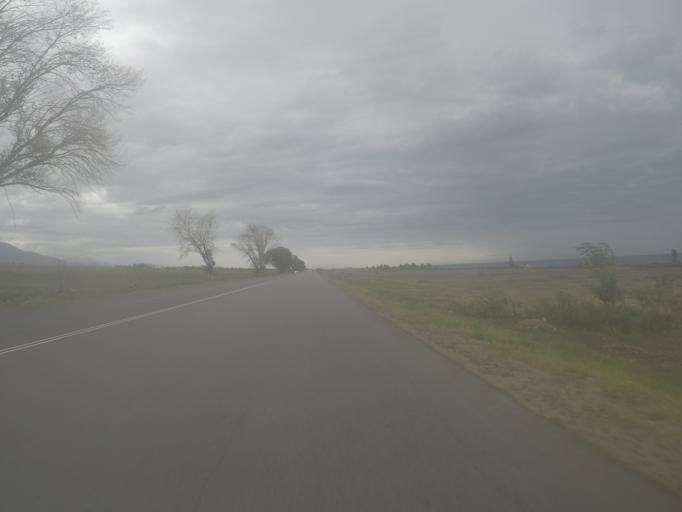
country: KG
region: Ysyk-Koel
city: Cholpon-Ata
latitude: 42.5985
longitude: 76.7970
